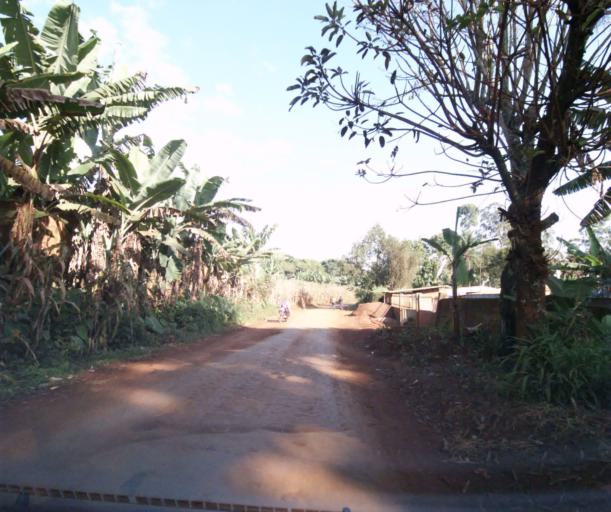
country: CM
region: West
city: Mbouda
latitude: 5.6115
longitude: 10.2884
